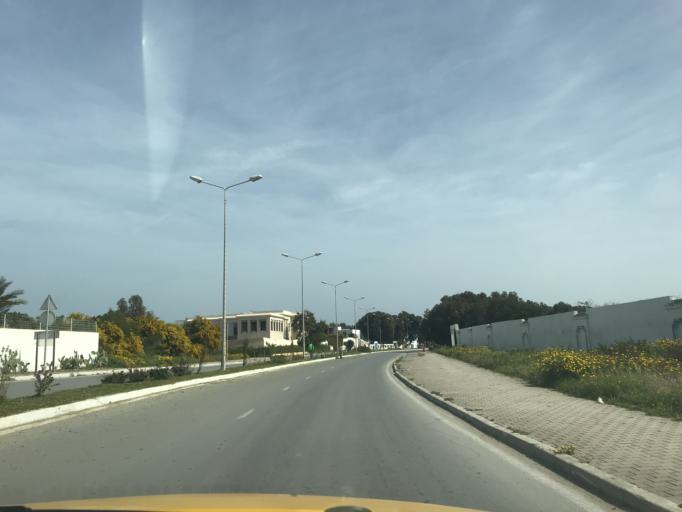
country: TN
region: Tunis
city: Al Marsa
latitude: 36.9189
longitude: 10.2823
